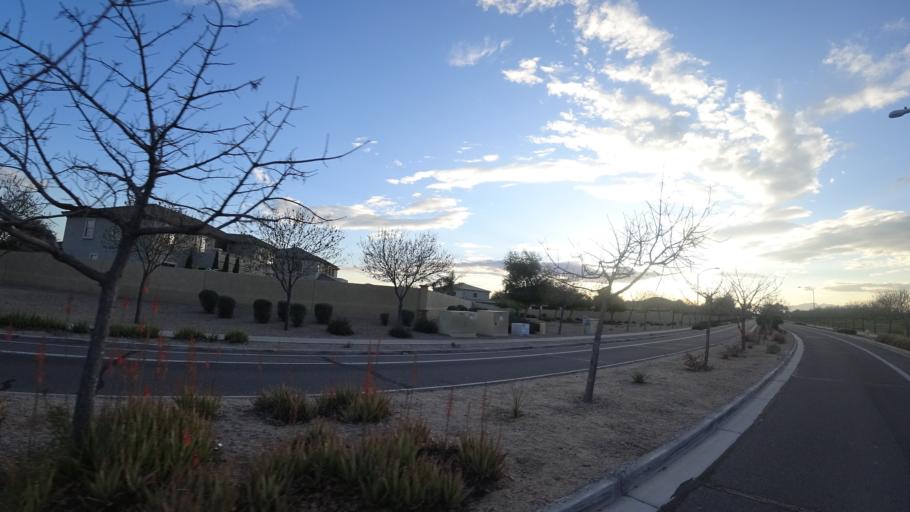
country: US
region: Arizona
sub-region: Maricopa County
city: Peoria
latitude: 33.5448
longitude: -112.2456
